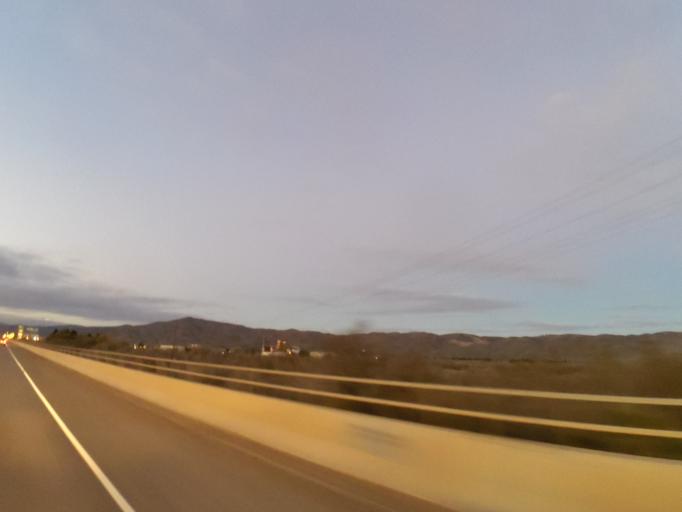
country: US
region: California
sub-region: Monterey County
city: Soledad
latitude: 36.4079
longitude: -121.3186
